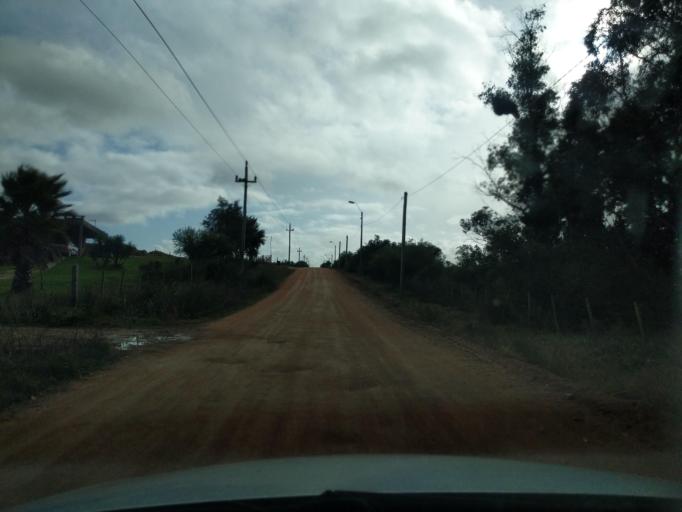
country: UY
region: Florida
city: Florida
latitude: -34.0667
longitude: -56.2190
